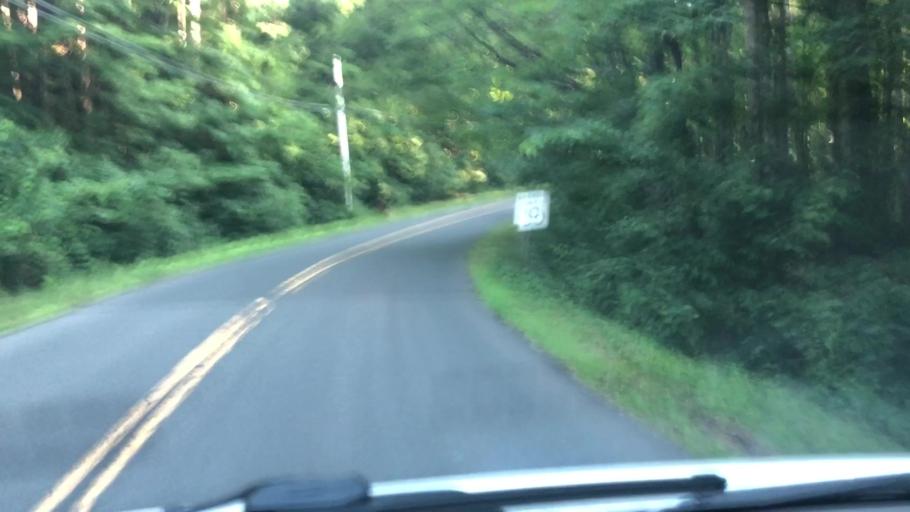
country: US
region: Massachusetts
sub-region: Hampshire County
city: Williamsburg
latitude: 42.3398
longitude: -72.7252
